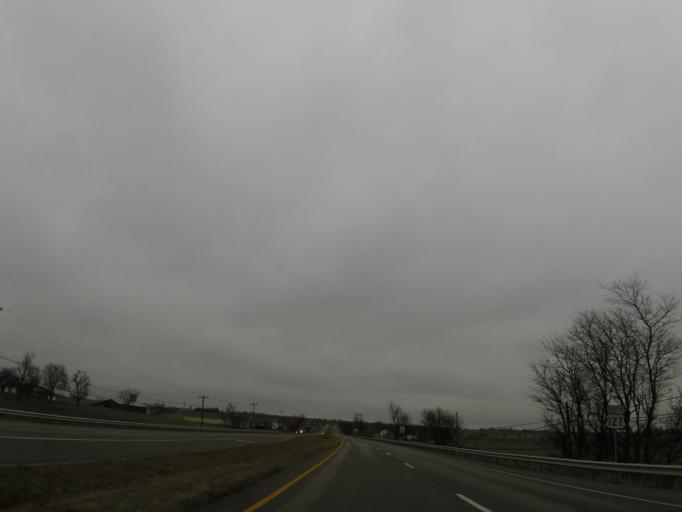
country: US
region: Kentucky
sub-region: Mercer County
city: Jackson
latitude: 37.8495
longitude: -84.8519
